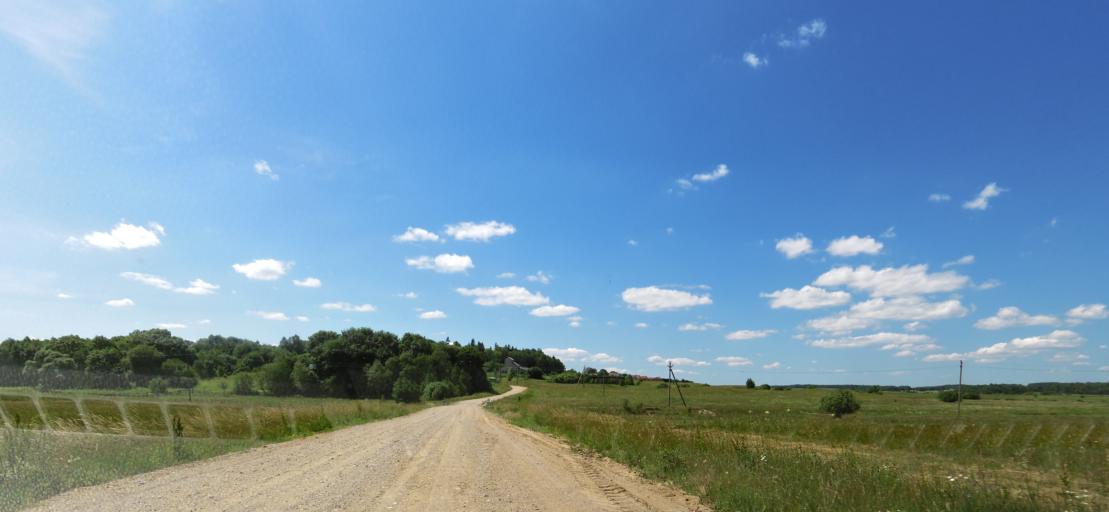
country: LT
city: Nemencine
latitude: 54.9017
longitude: 25.4878
